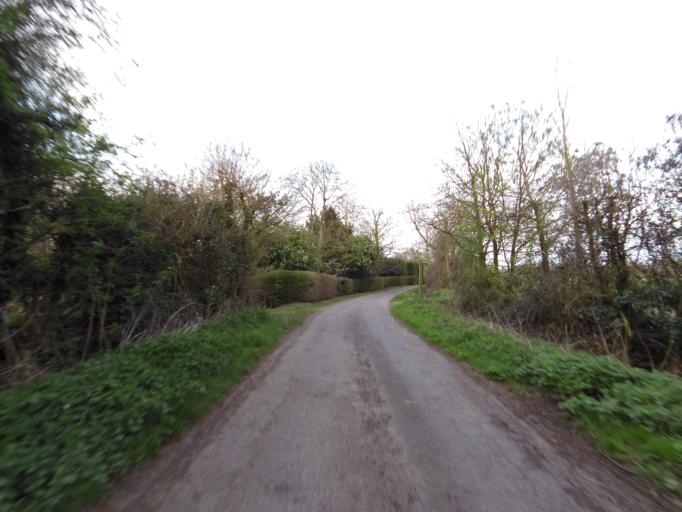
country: GB
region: England
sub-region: Suffolk
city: Kesgrave
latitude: 52.1480
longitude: 1.2312
